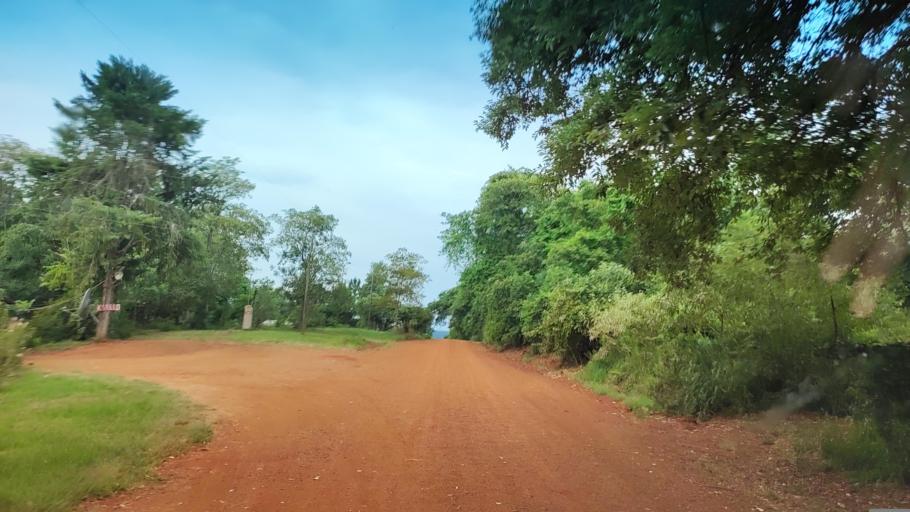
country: AR
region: Misiones
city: Gobernador Roca
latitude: -27.1521
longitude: -55.4843
